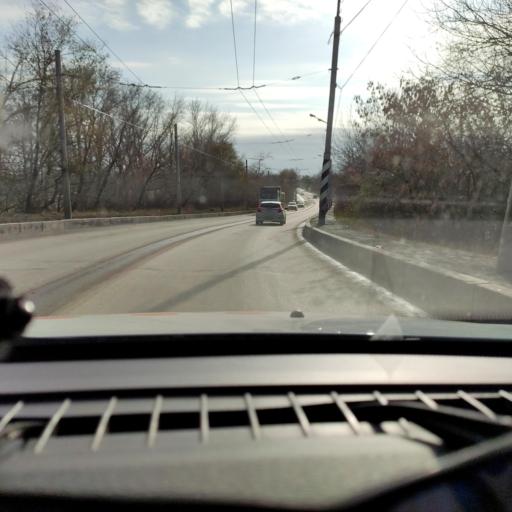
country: RU
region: Samara
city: Samara
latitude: 53.1504
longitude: 50.0938
